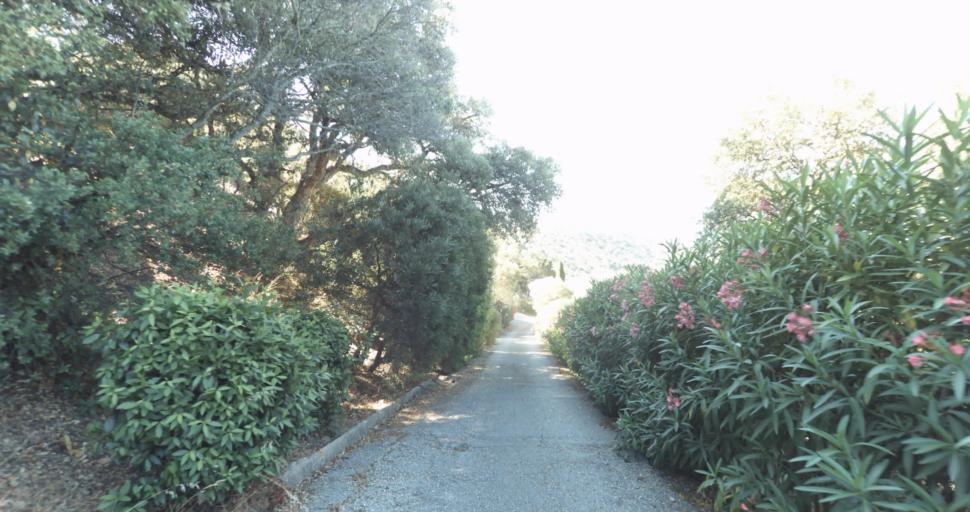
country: FR
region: Provence-Alpes-Cote d'Azur
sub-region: Departement du Var
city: Ramatuelle
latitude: 43.2183
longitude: 6.5999
